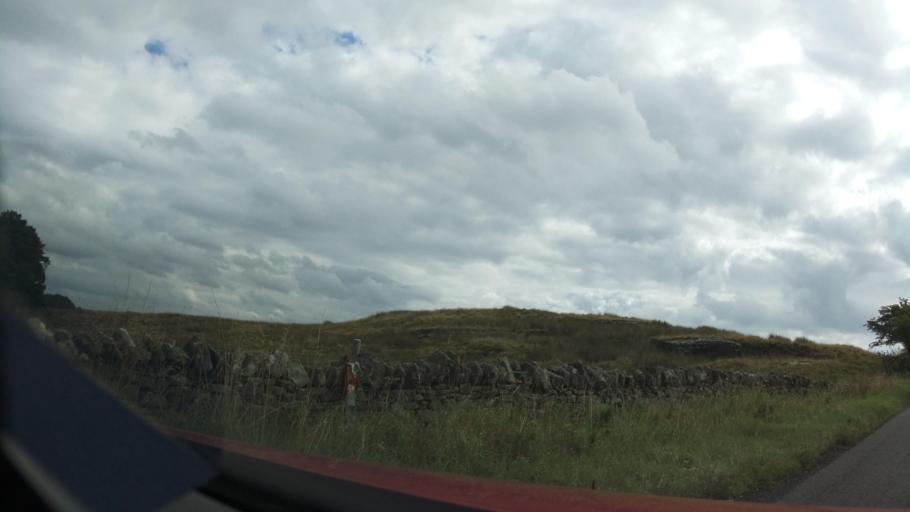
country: GB
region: England
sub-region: Northumberland
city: Birtley
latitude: 55.0935
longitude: -2.1148
